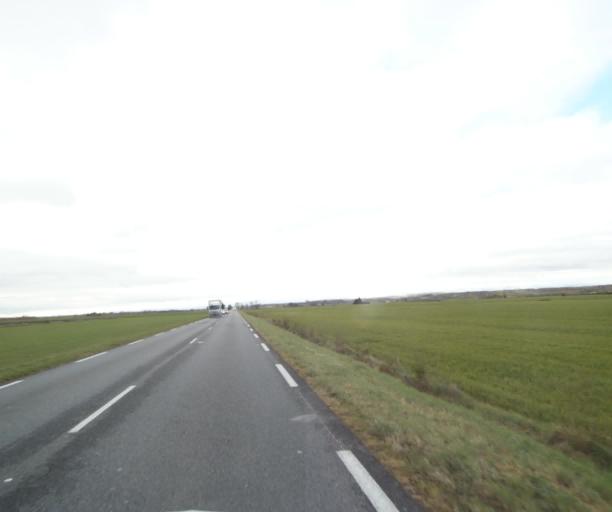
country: FR
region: Midi-Pyrenees
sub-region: Departement de l'Ariege
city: Saverdun
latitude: 43.2685
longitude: 1.5531
